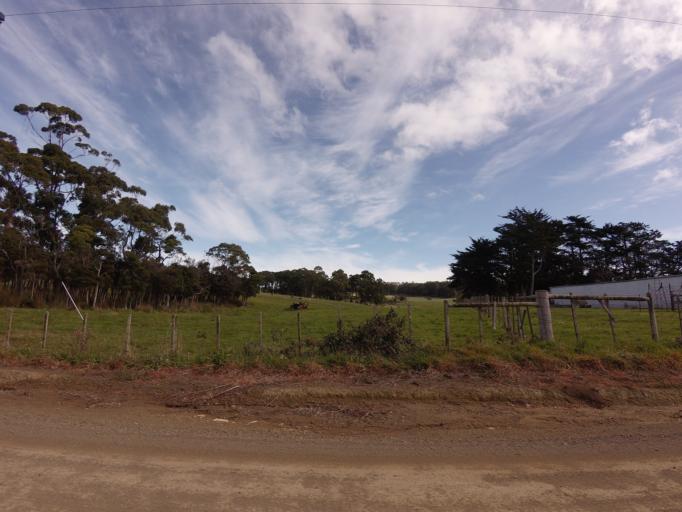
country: AU
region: Tasmania
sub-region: Clarence
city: Sandford
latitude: -43.1559
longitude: 147.7650
